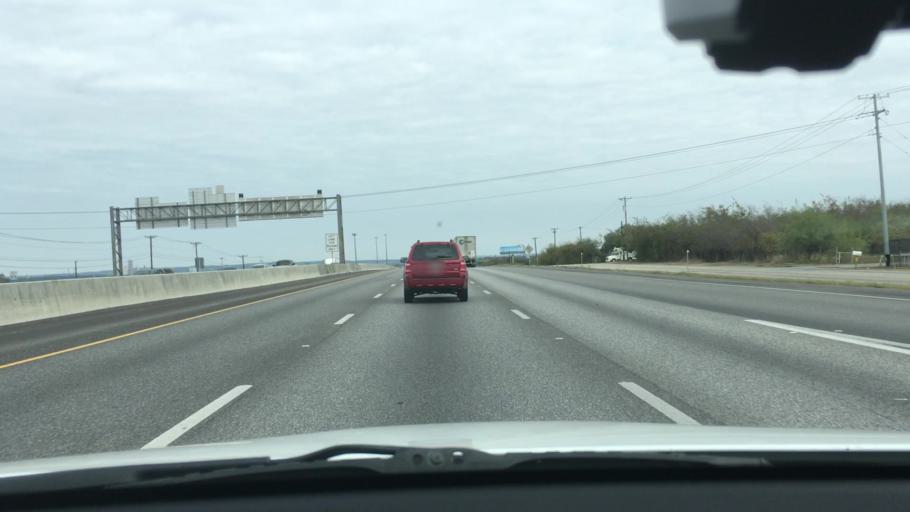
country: US
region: Texas
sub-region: Guadalupe County
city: Lake Dunlap
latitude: 29.7495
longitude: -98.0559
